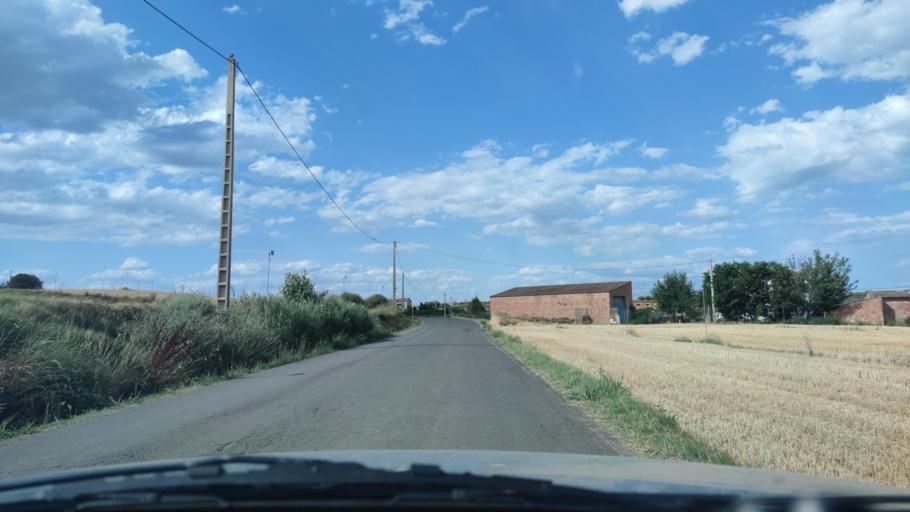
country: ES
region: Catalonia
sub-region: Provincia de Lleida
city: Alcarras
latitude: 41.5738
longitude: 0.5316
